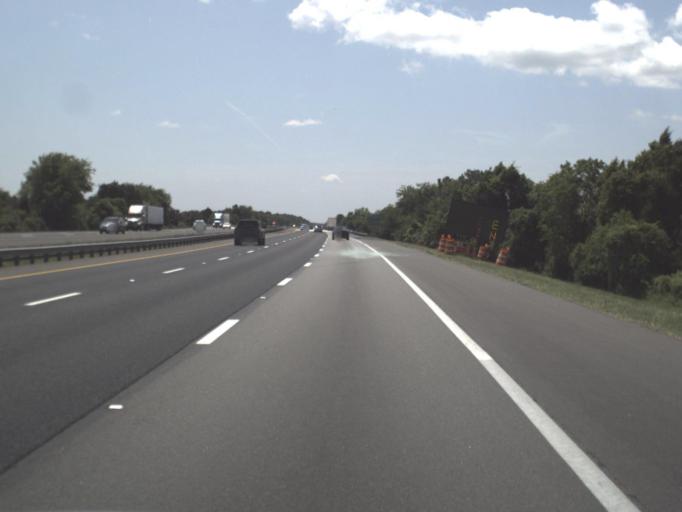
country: US
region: Florida
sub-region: Nassau County
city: Yulee
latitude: 30.5789
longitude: -81.6468
